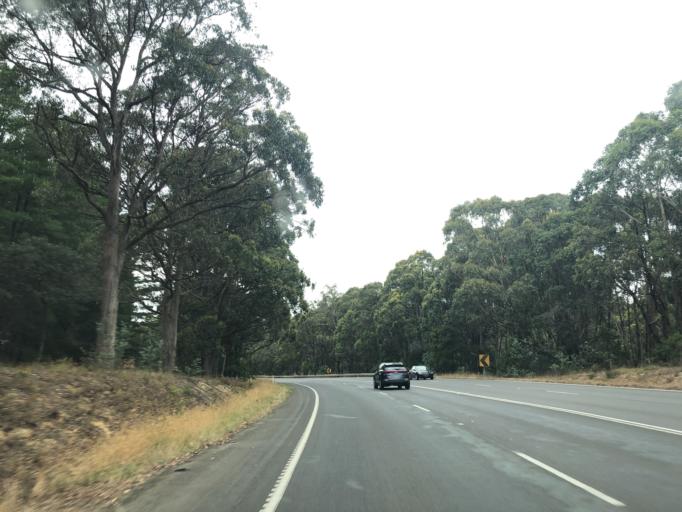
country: AU
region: Victoria
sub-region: Hume
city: Sunbury
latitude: -37.3988
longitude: 144.5292
